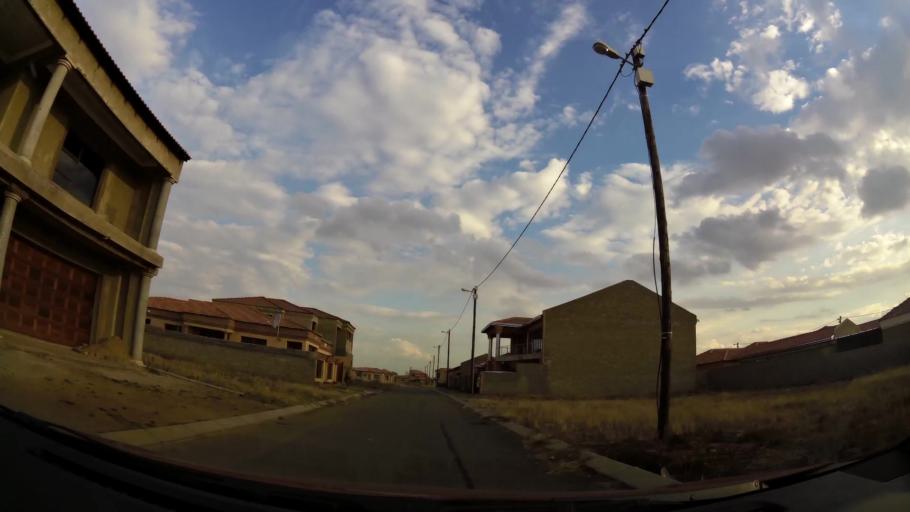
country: ZA
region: Gauteng
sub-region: Sedibeng District Municipality
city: Vanderbijlpark
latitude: -26.6090
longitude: 27.8152
